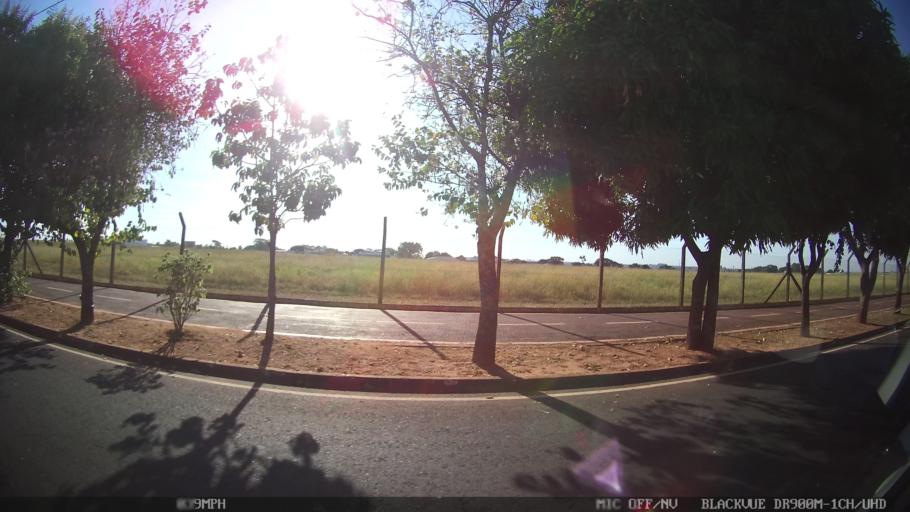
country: BR
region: Sao Paulo
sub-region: Sao Jose Do Rio Preto
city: Sao Jose do Rio Preto
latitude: -20.8192
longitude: -49.4077
